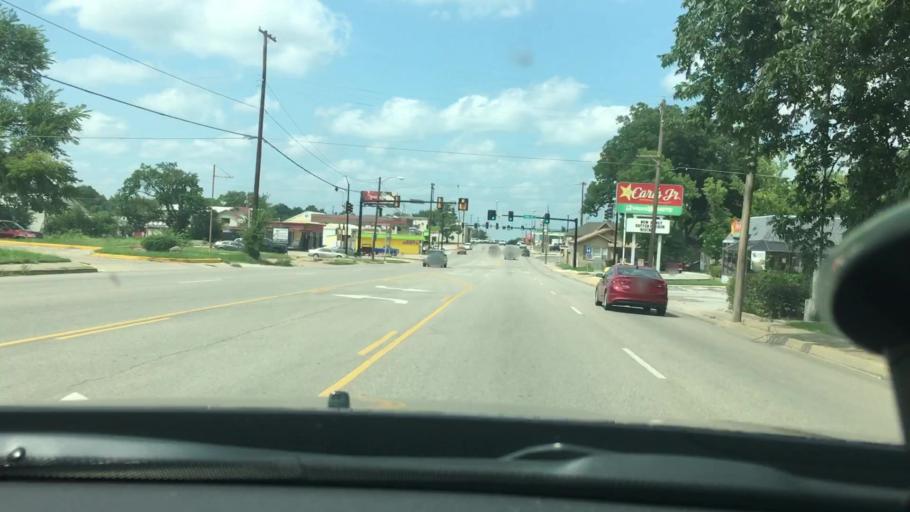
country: US
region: Oklahoma
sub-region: Pontotoc County
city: Ada
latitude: 34.7724
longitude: -96.6699
